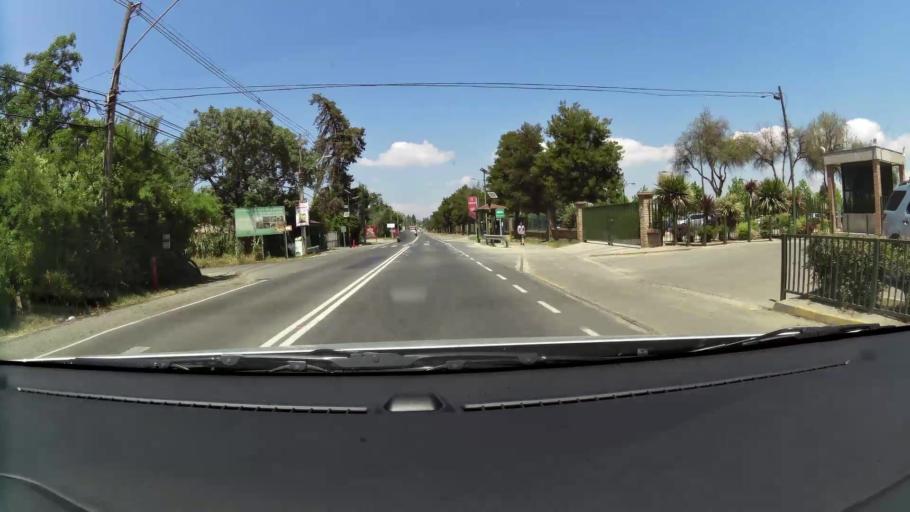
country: CL
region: Santiago Metropolitan
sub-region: Provincia de Maipo
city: San Bernardo
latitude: -33.5842
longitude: -70.7769
